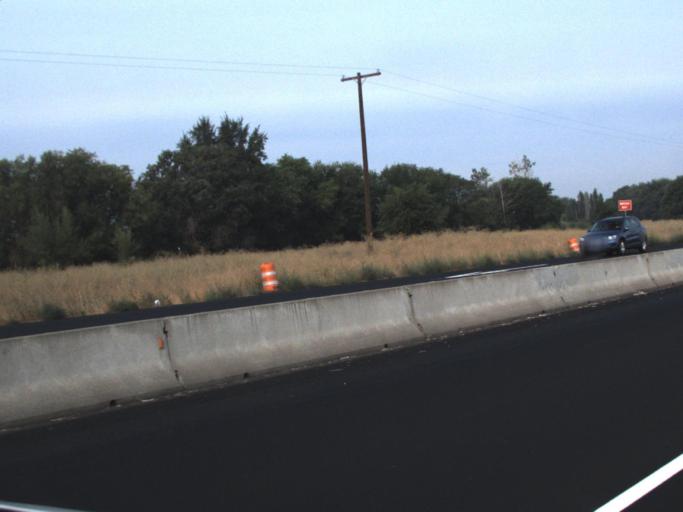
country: US
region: Washington
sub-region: Yakima County
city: Wapato
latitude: 46.4110
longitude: -120.3878
